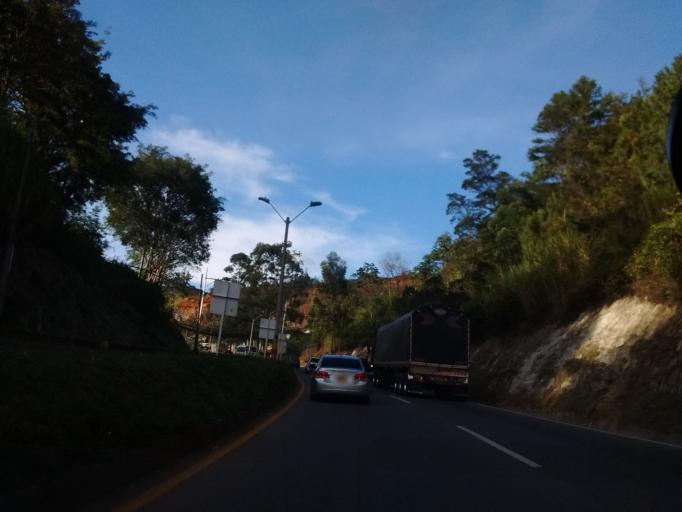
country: CO
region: Antioquia
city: Bello
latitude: 6.3154
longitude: -75.5476
